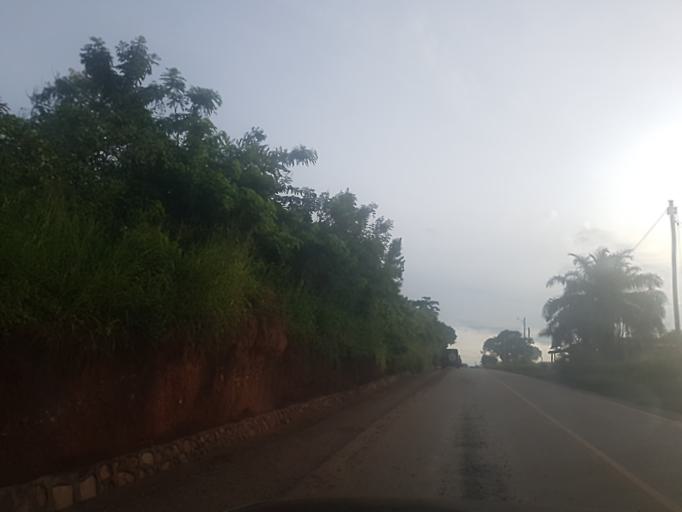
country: UG
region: Central Region
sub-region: Wakiso District
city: Bweyogerere
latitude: 0.3970
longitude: 32.6702
